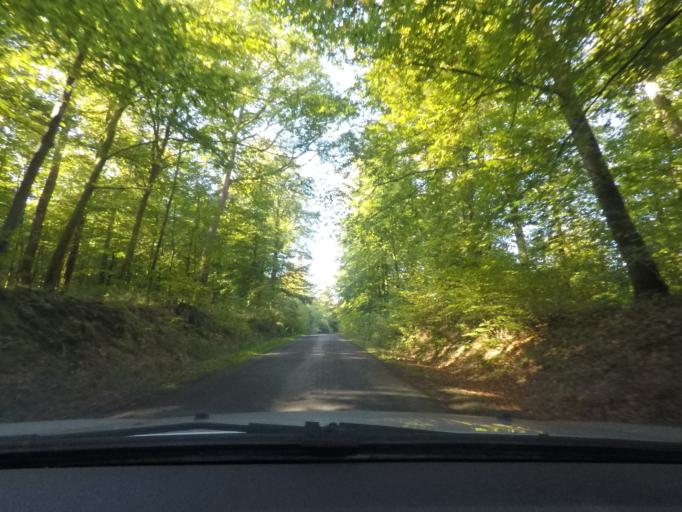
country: BE
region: Wallonia
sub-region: Province du Luxembourg
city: Messancy
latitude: 49.6294
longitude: 5.7461
